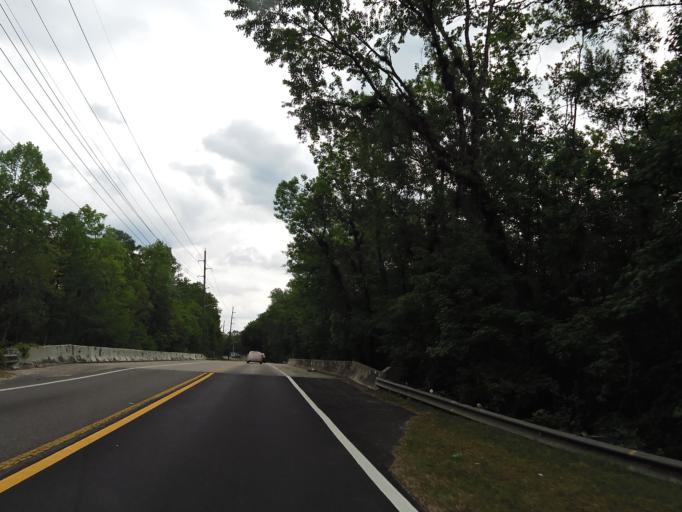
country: US
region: Florida
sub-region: Clay County
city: Bellair-Meadowbrook Terrace
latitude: 30.2015
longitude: -81.7312
